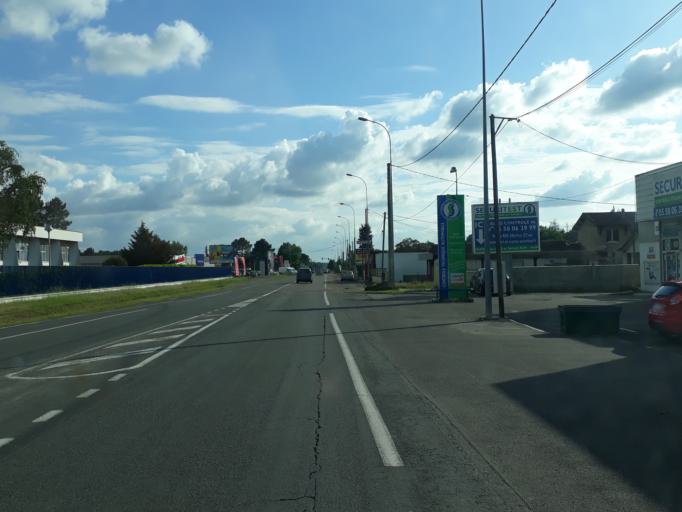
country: FR
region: Aquitaine
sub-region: Departement des Landes
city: Mont-de-Marsan
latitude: 43.9082
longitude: -0.4695
